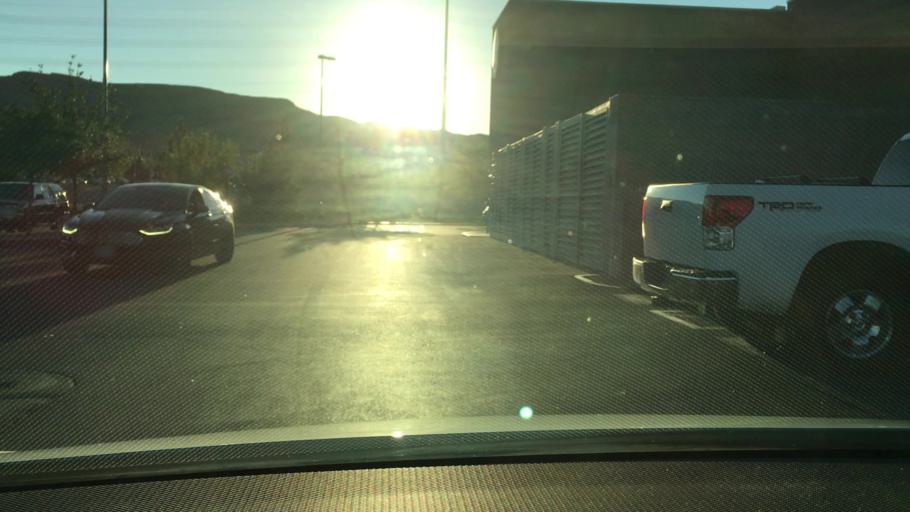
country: US
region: Nevada
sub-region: Clark County
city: Summerlin South
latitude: 36.1455
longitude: -115.3352
